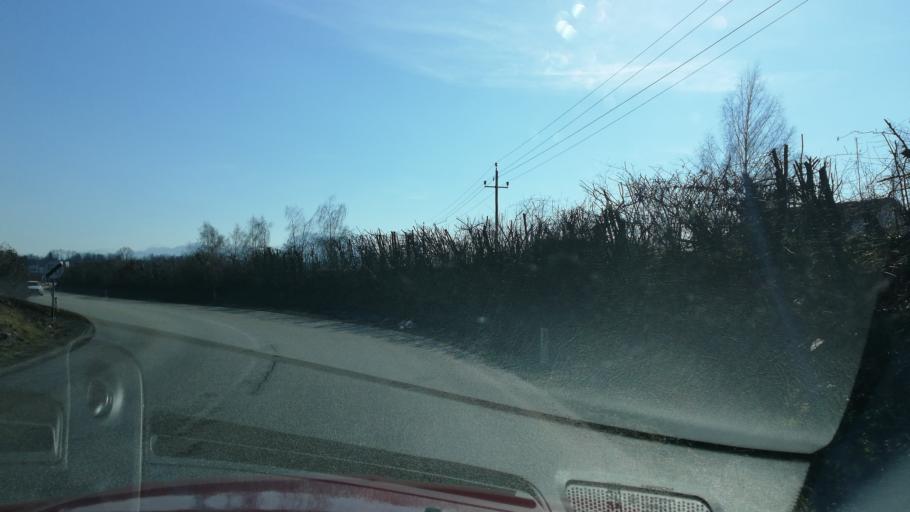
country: AT
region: Upper Austria
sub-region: Politischer Bezirk Vocklabruck
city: Redlham
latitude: 48.0218
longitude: 13.7393
